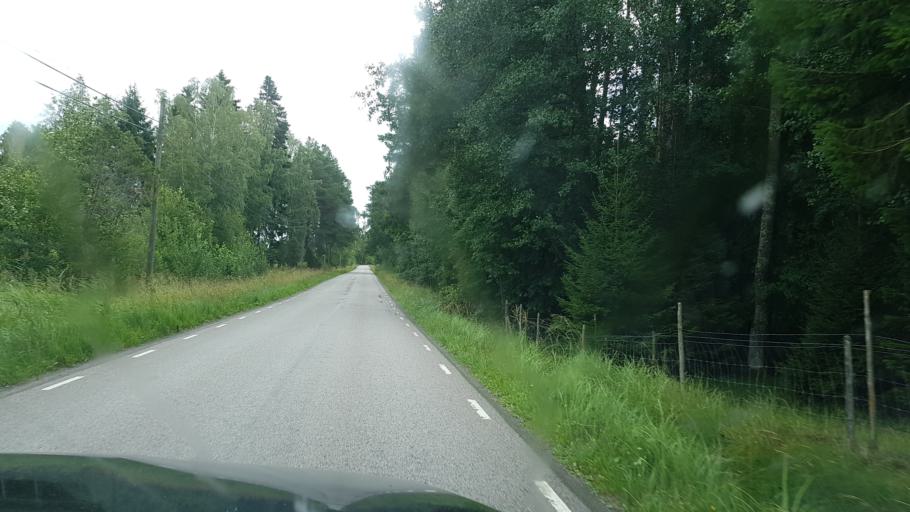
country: SE
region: Uppsala
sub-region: Osthammars Kommun
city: Oregrund
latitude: 60.3635
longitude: 18.4346
